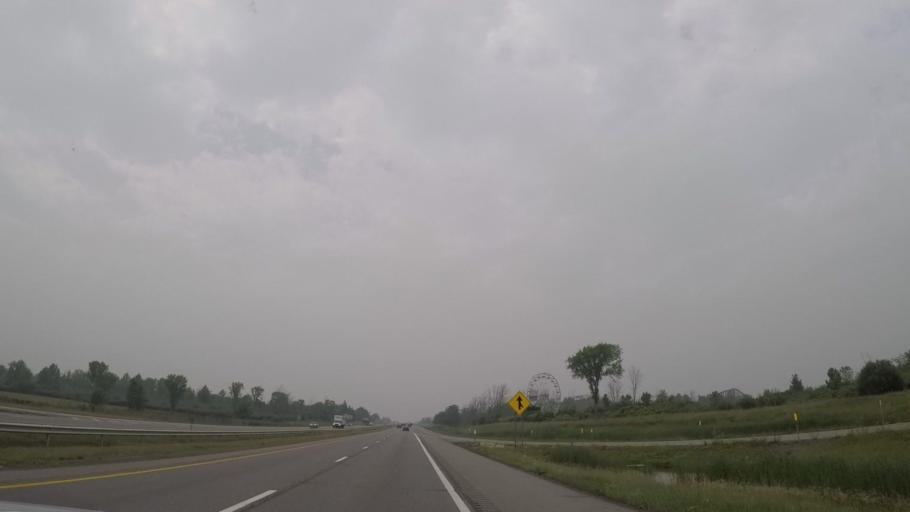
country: US
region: New York
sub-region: Erie County
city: Grandyle Village
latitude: 43.0233
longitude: -78.9754
